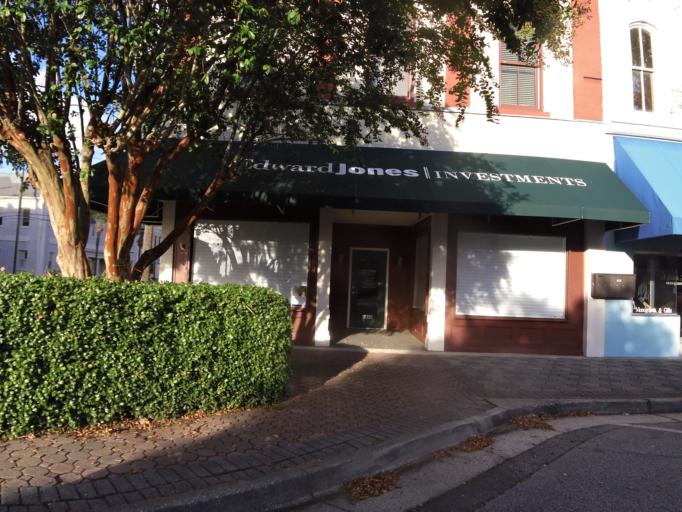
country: US
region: Georgia
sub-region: Glynn County
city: Brunswick
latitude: 31.1490
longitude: -81.4952
